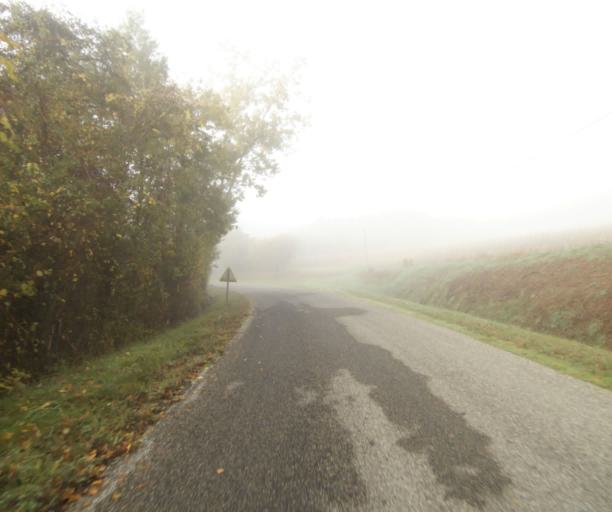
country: FR
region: Midi-Pyrenees
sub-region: Departement de la Haute-Garonne
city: Villemur-sur-Tarn
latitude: 43.8878
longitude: 1.4891
